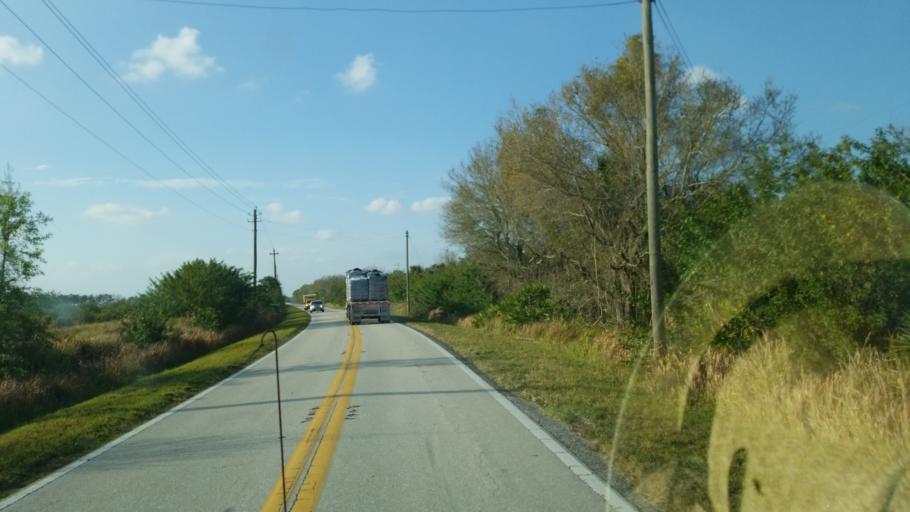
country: US
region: Florida
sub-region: Hardee County
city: Bowling Green
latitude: 27.7224
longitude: -81.9631
